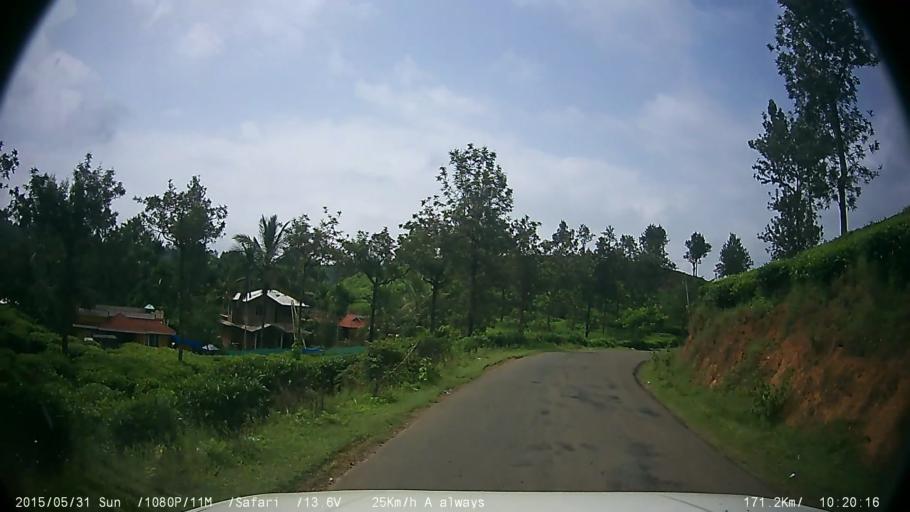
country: IN
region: Kerala
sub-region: Wayanad
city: Kalpetta
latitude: 11.5466
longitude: 76.1379
